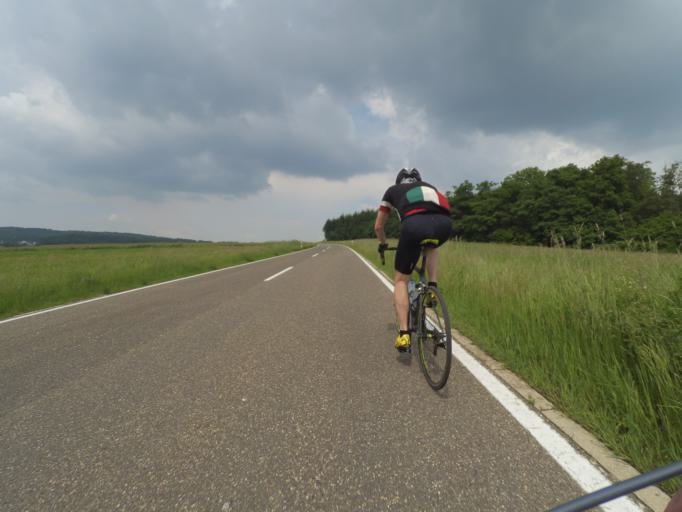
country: DE
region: Rheinland-Pfalz
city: Lieg
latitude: 50.1500
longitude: 7.3386
